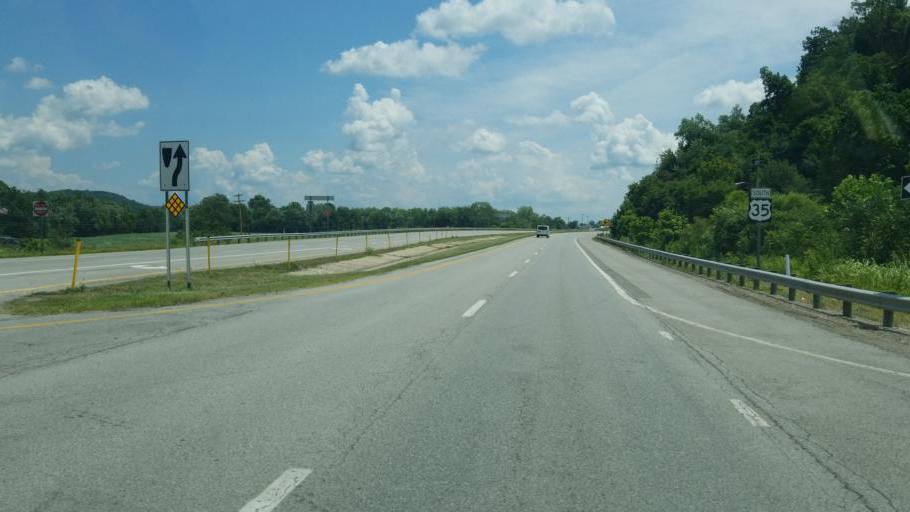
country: US
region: West Virginia
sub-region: Mason County
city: Point Pleasant
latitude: 38.8183
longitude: -82.1174
